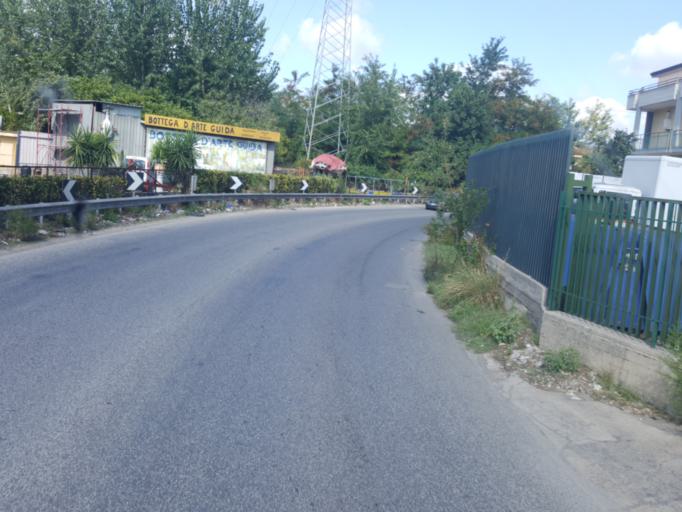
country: IT
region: Campania
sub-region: Provincia di Napoli
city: Nola
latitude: 40.9184
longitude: 14.5151
